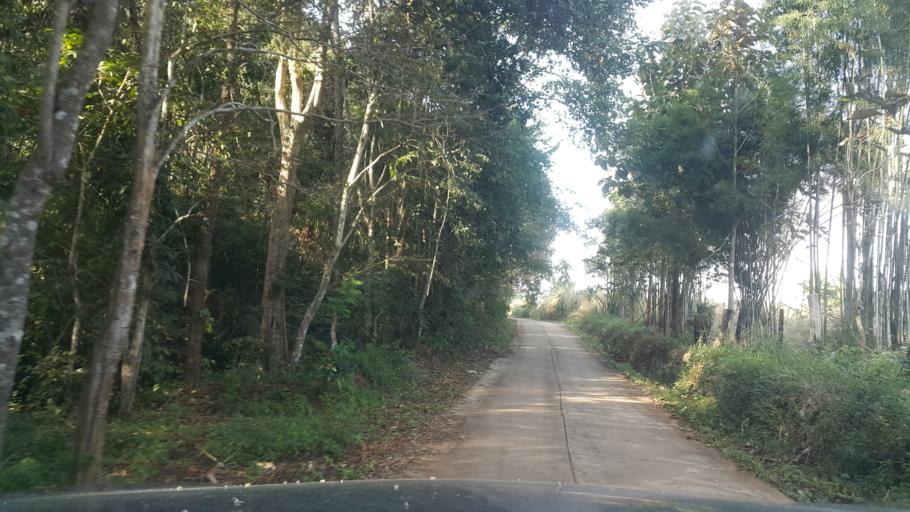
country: TH
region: Chiang Mai
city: Samoeng
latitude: 18.9800
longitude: 98.6837
